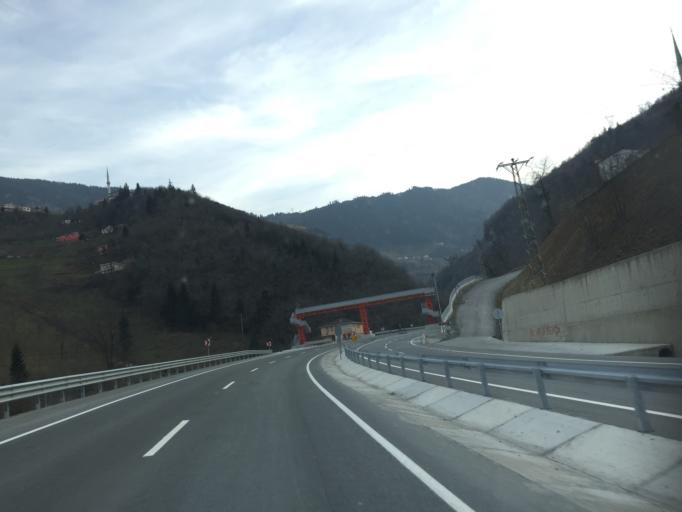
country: TR
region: Trabzon
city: Macka
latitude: 40.7615
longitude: 39.5632
